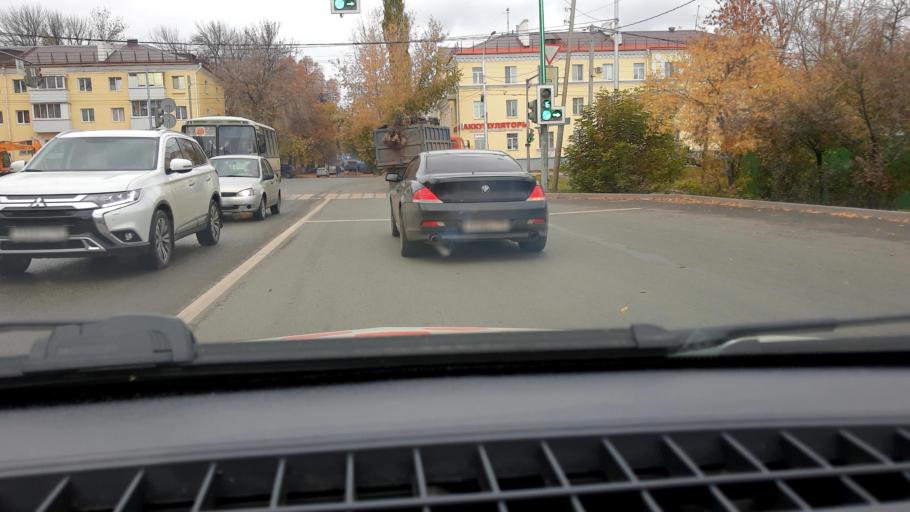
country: RU
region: Bashkortostan
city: Ufa
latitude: 54.8226
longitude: 56.1119
